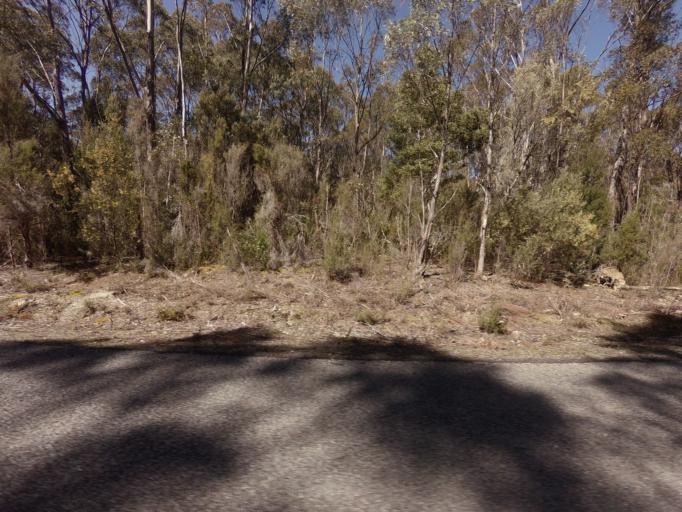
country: AU
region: Tasmania
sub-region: Huon Valley
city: Geeveston
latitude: -42.7658
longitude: 146.3971
